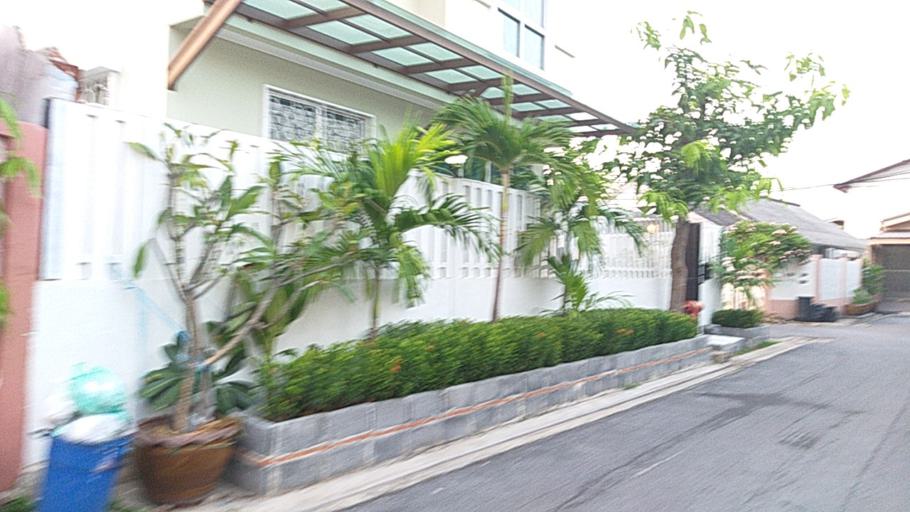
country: TH
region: Bangkok
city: Lat Phrao
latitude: 13.8287
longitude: 100.6196
